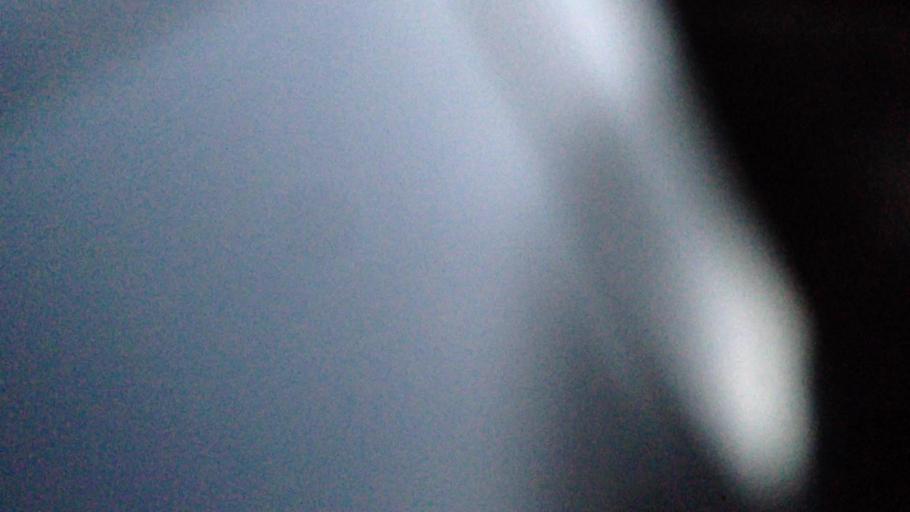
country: US
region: New York
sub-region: Columbia County
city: Lorenz Park
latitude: 42.2720
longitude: -73.7663
